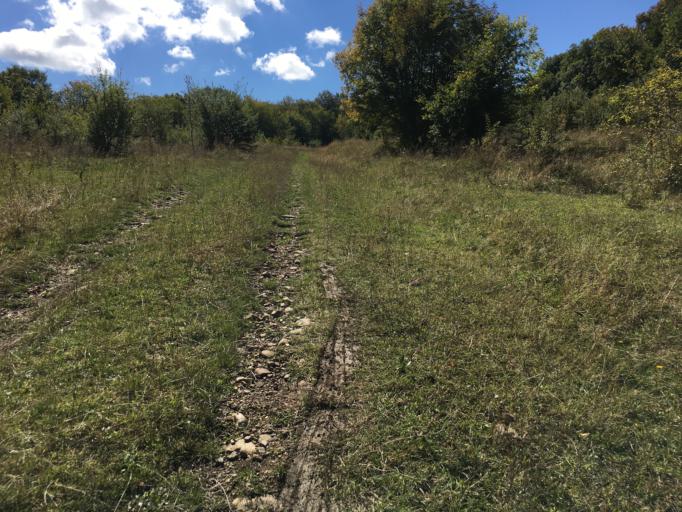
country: GE
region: Mtskheta-Mtianeti
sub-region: Tianetis Munitsip'alit'et'i
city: T'ianet'i
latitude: 41.9343
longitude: 44.9755
